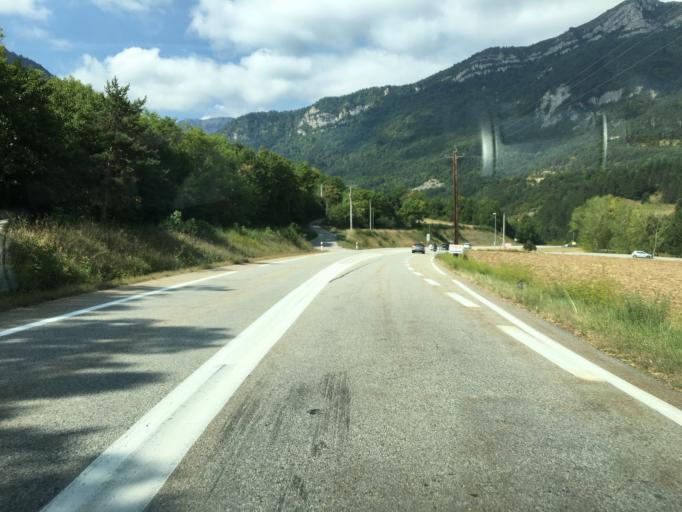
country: FR
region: Rhone-Alpes
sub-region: Departement de l'Isere
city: Mens
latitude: 44.7875
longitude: 5.6399
